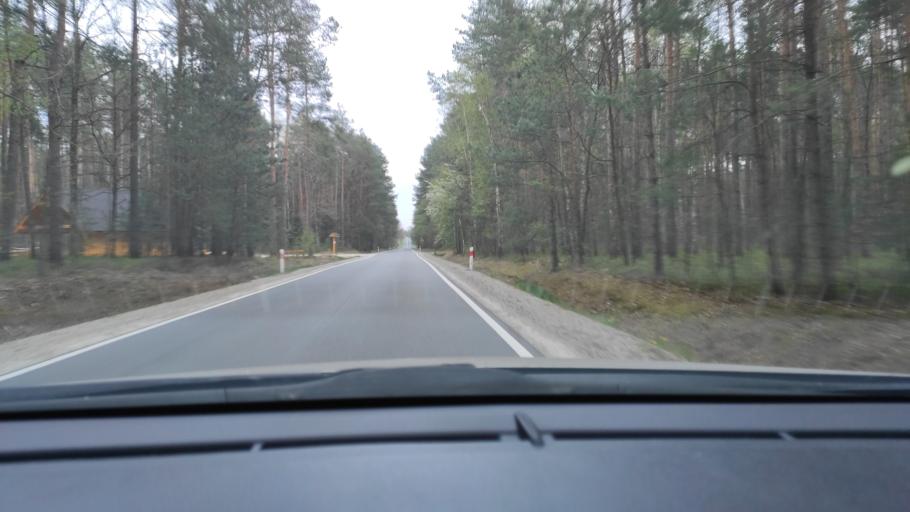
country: PL
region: Masovian Voivodeship
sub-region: Powiat zwolenski
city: Zwolen
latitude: 51.3903
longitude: 21.5495
